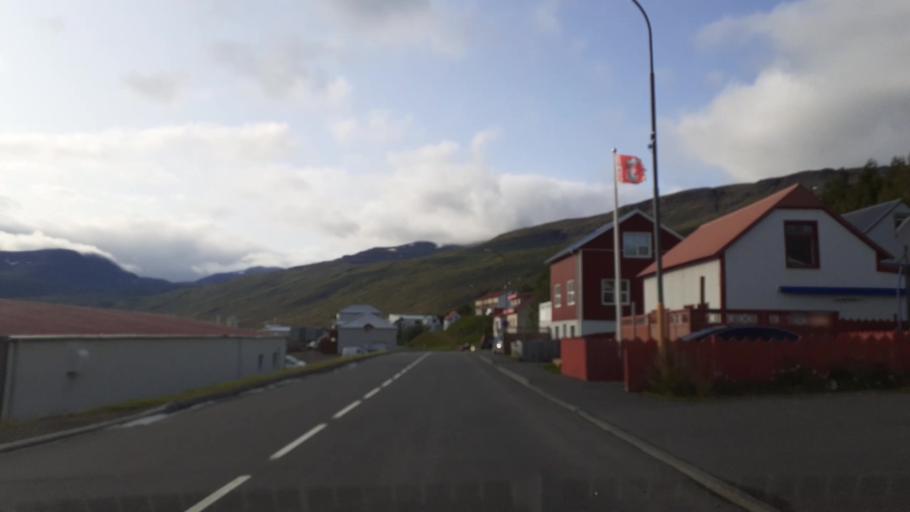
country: IS
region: East
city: Eskifjoerdur
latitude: 65.0679
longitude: -14.0061
